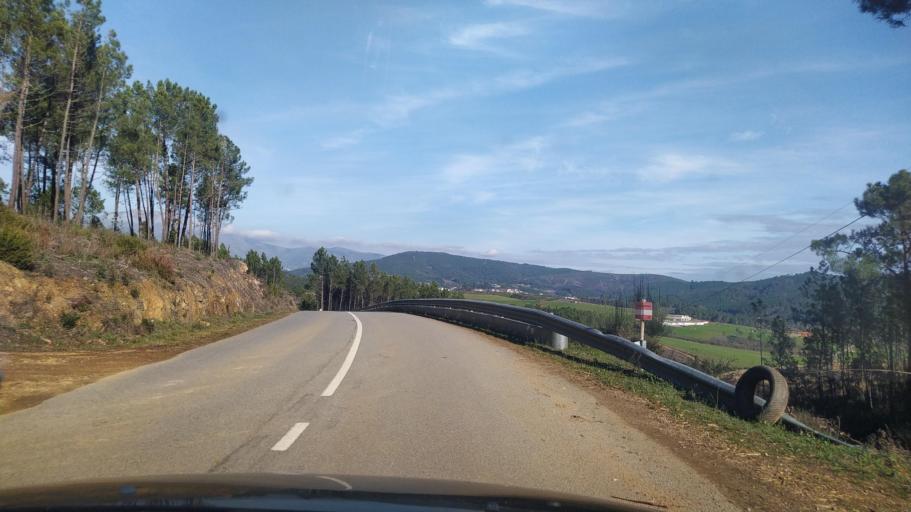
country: PT
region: Castelo Branco
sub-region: Concelho do Fundao
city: Aldeia de Joanes
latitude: 40.1787
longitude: -7.6631
